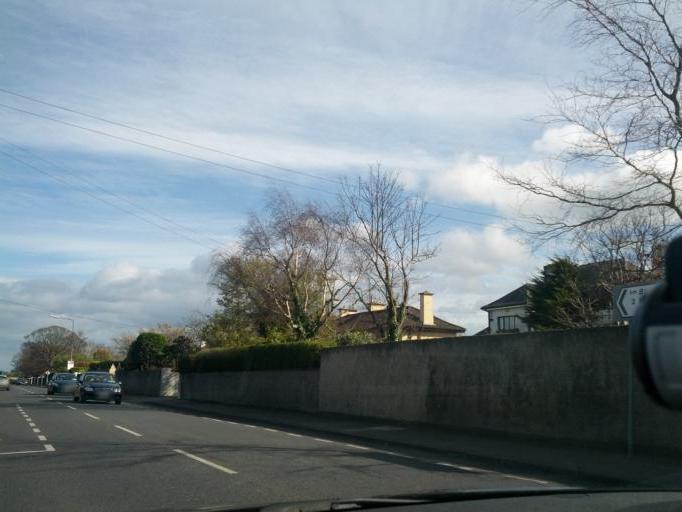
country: IE
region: Leinster
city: Sutton
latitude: 53.3910
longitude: -6.0912
